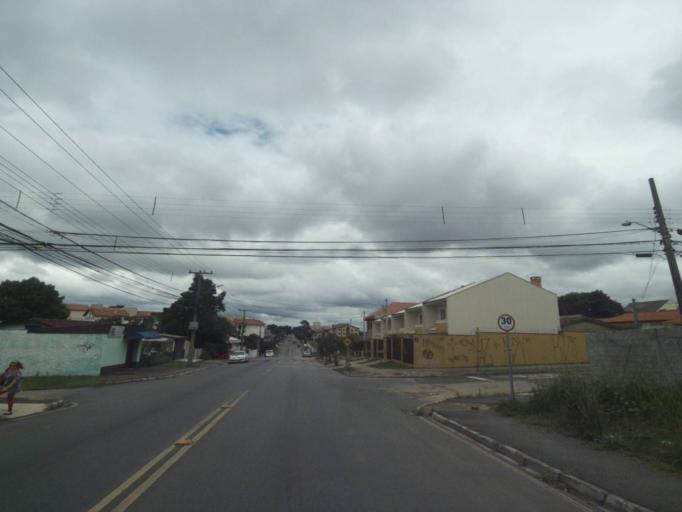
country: BR
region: Parana
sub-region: Curitiba
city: Curitiba
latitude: -25.4926
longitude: -49.3022
